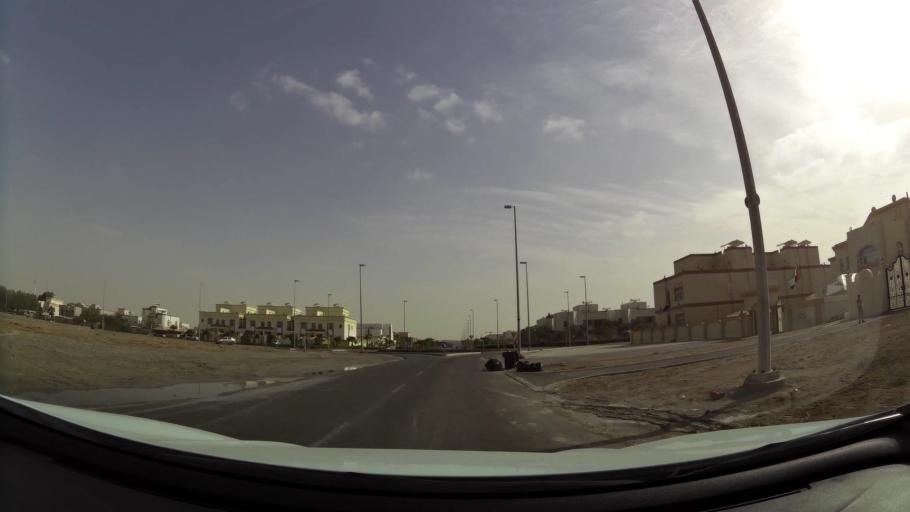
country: AE
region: Abu Dhabi
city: Abu Dhabi
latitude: 24.4118
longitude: 54.5780
